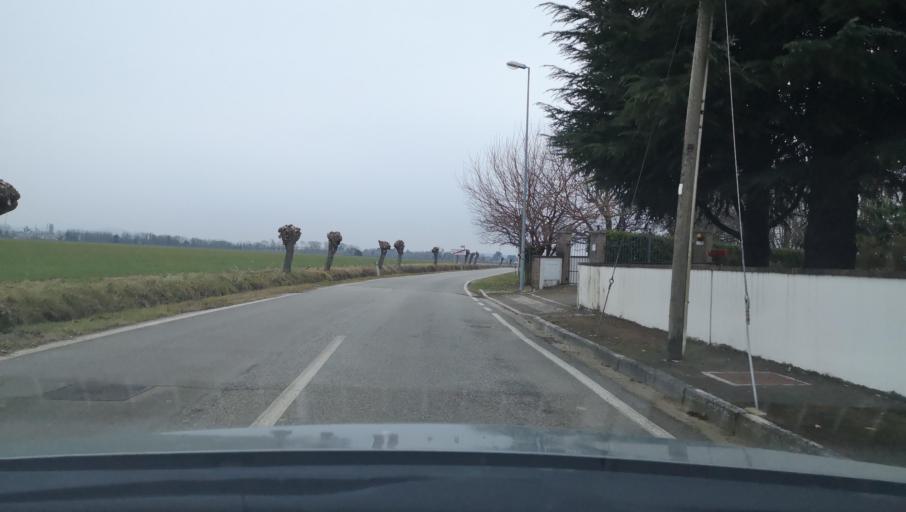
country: IT
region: Friuli Venezia Giulia
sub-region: Provincia di Udine
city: Trivignano Udinese
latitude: 45.9535
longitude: 13.3238
